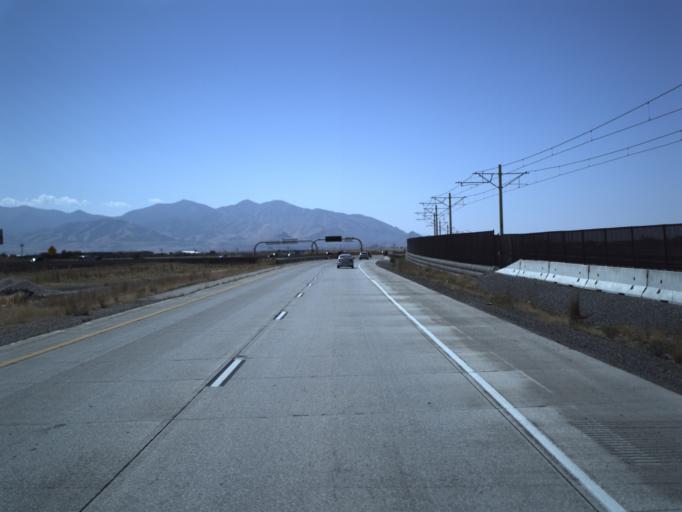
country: US
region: Utah
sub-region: Salt Lake County
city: Salt Lake City
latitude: 40.7660
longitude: -111.9638
